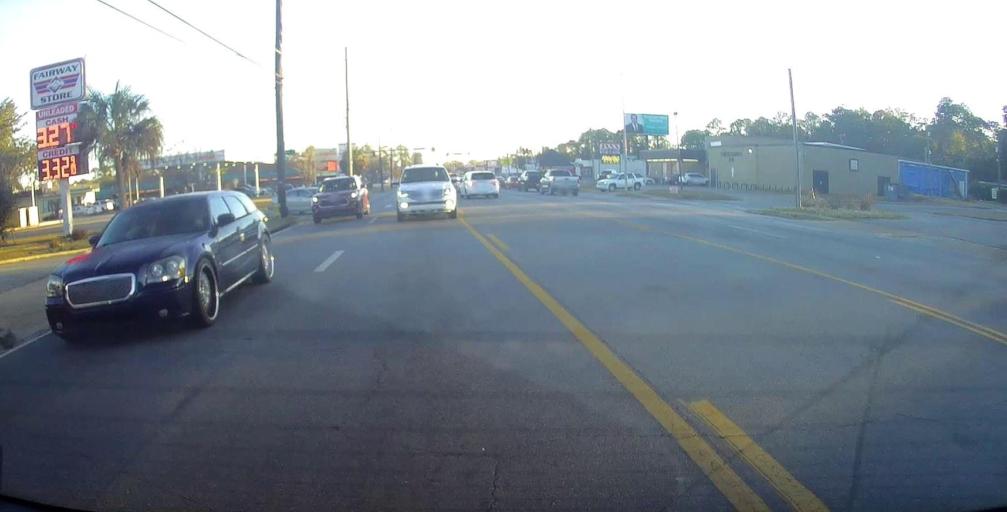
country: US
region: Georgia
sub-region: Dougherty County
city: Albany
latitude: 31.5691
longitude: -84.1762
